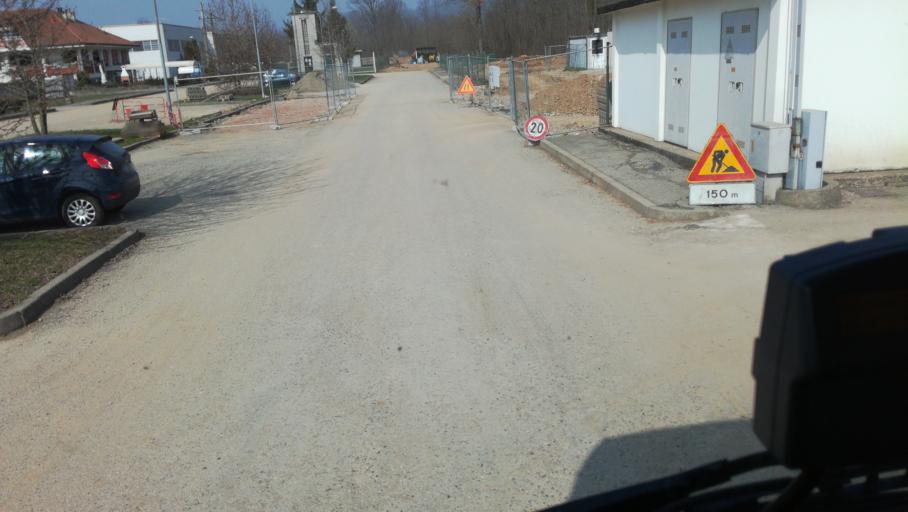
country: IT
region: Piedmont
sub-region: Provincia di Novara
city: Grignasco
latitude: 45.6737
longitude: 8.3510
